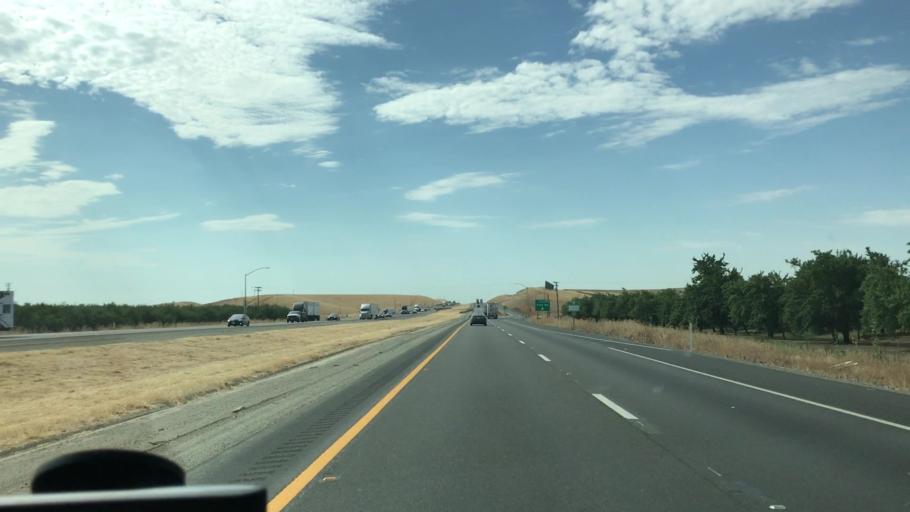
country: US
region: California
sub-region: Stanislaus County
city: Patterson
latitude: 37.4013
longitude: -121.1412
